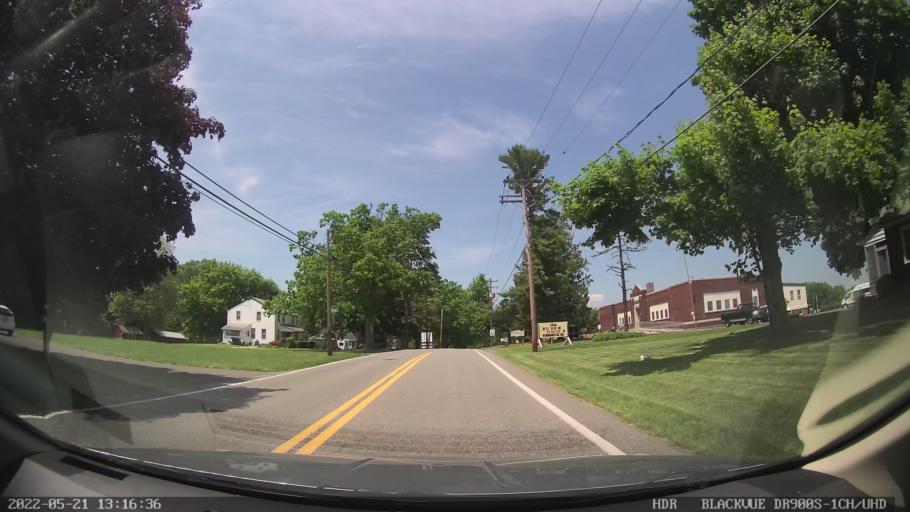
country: US
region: Pennsylvania
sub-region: Montgomery County
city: Gilbertsville
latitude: 40.3521
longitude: -75.5861
